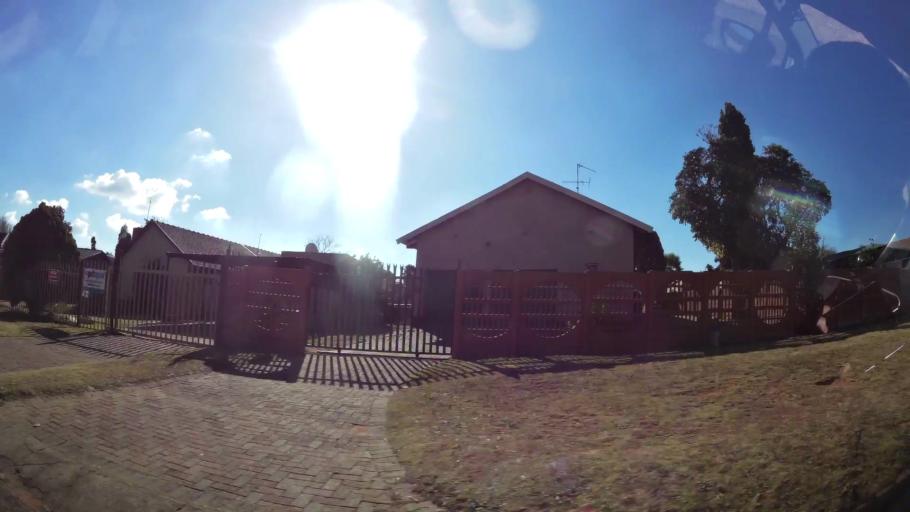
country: ZA
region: Gauteng
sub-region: City of Johannesburg Metropolitan Municipality
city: Roodepoort
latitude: -26.1405
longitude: 27.8244
